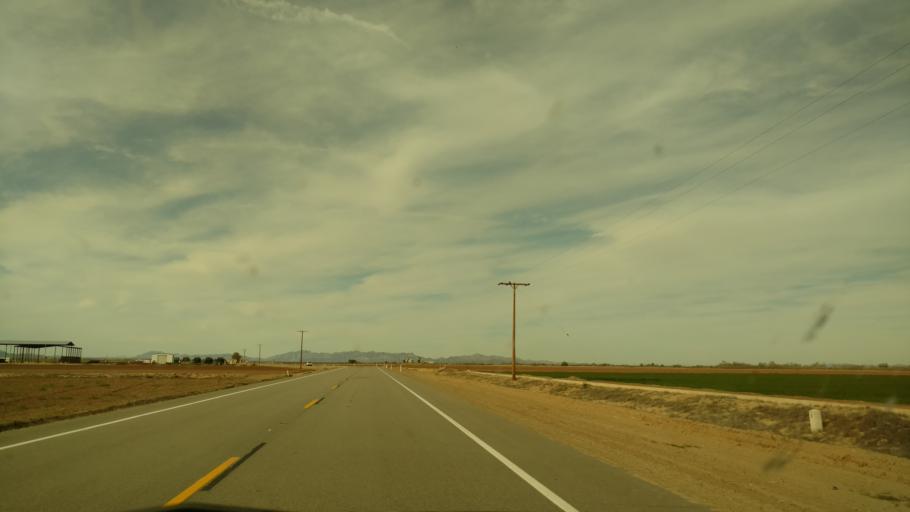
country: US
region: California
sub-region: Riverside County
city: Mesa Verde
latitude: 33.4510
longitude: -114.7312
